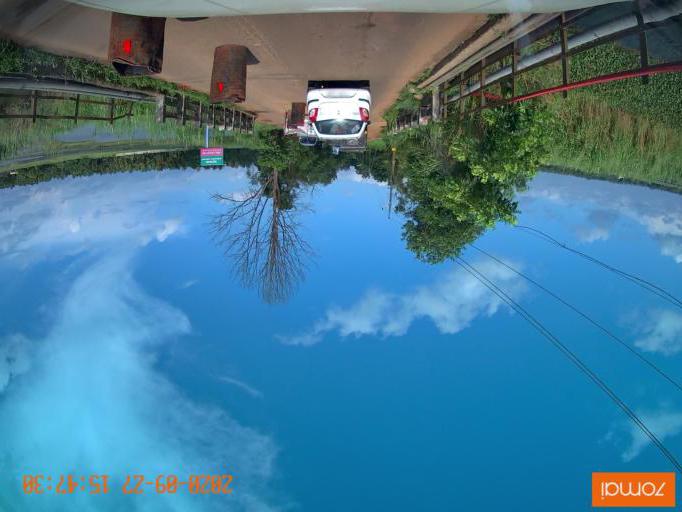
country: IN
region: Kerala
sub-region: Thrissur District
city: Thanniyam
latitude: 10.4821
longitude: 76.1293
